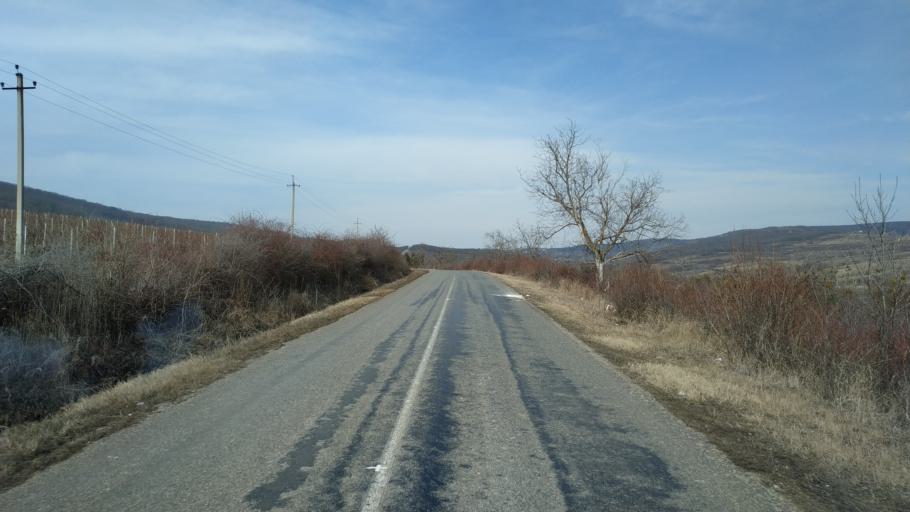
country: MD
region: Nisporeni
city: Nisporeni
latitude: 47.1755
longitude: 28.0863
